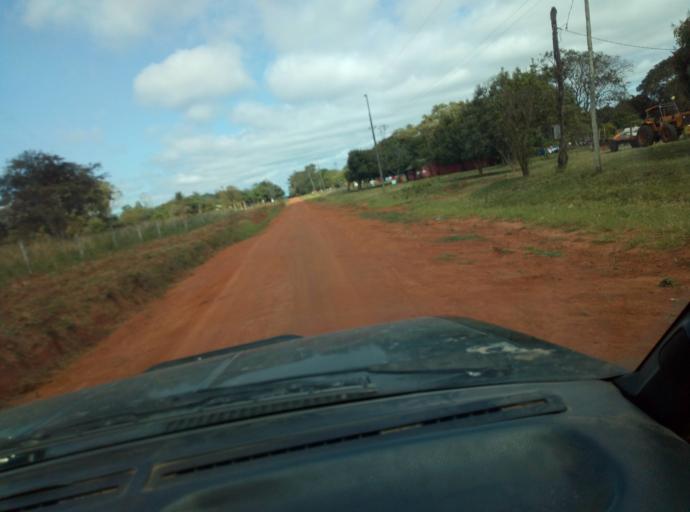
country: PY
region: Caaguazu
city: Doctor Cecilio Baez
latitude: -25.1525
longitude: -56.2911
